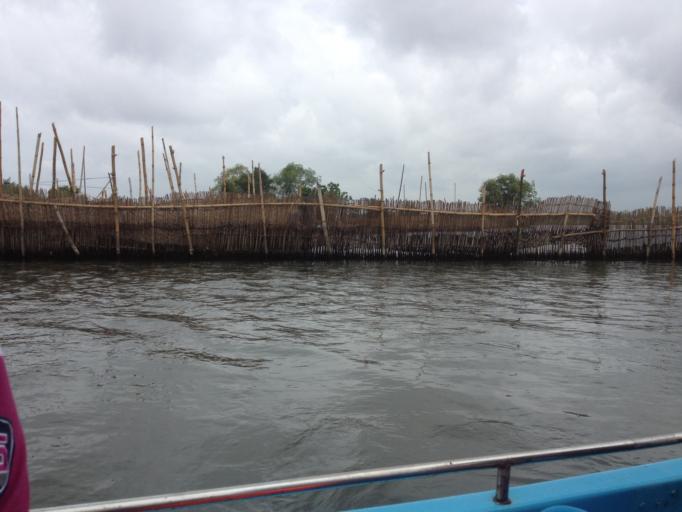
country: BJ
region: Mono
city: Come
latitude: 6.3764
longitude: 1.9452
